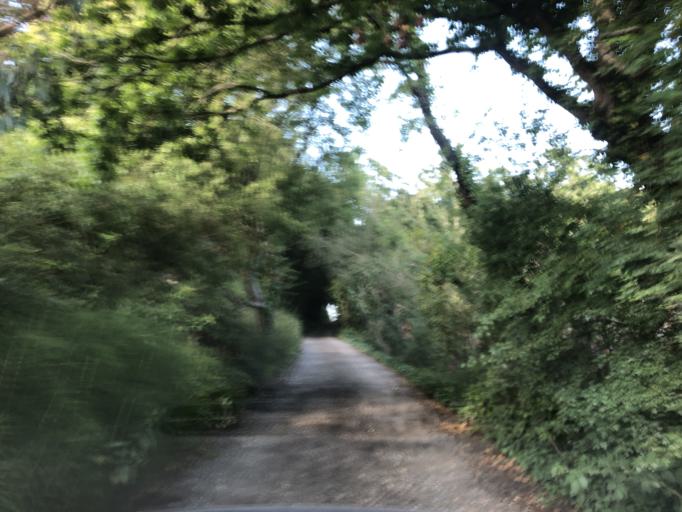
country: GB
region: England
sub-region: Isle of Wight
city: Shalfleet
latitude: 50.7150
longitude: -1.4476
